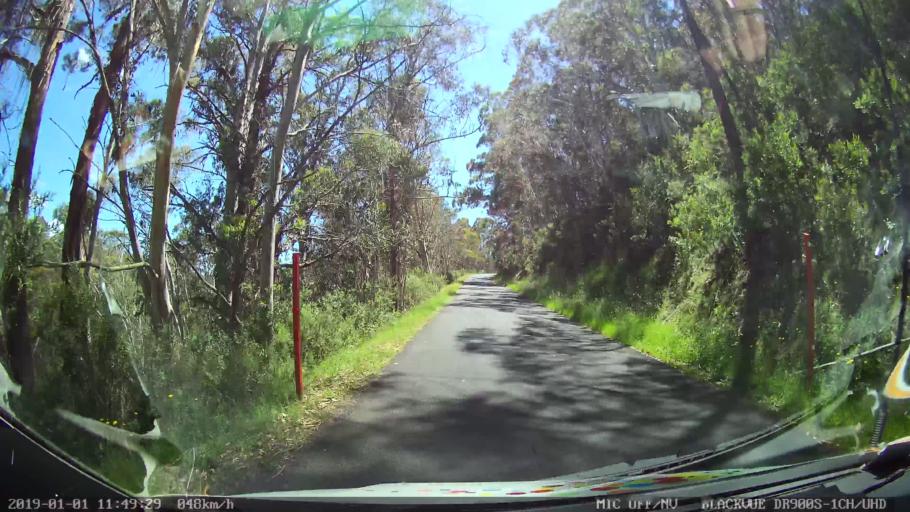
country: AU
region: New South Wales
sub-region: Snowy River
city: Jindabyne
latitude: -35.8934
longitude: 148.4134
